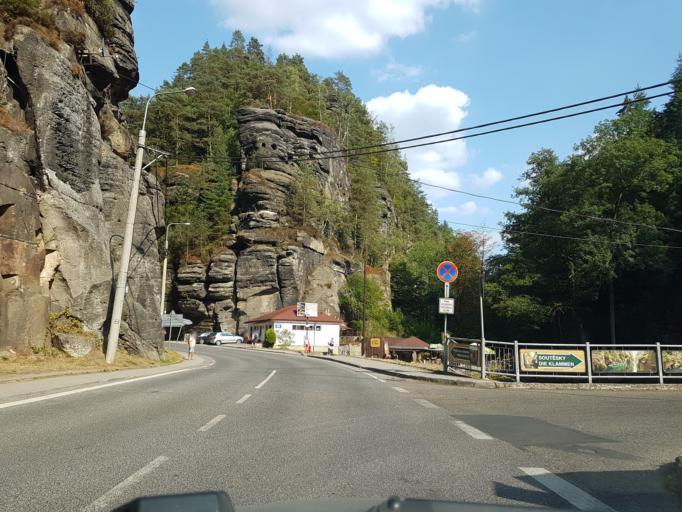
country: CZ
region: Ustecky
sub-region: Okres Decin
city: Decin
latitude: 50.8739
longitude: 14.2510
